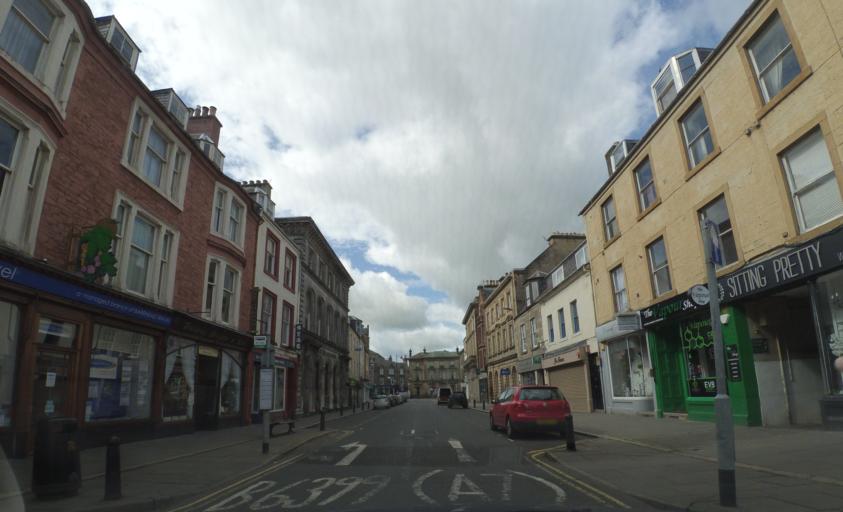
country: GB
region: Scotland
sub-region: The Scottish Borders
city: Hawick
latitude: 55.4222
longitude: -2.7873
